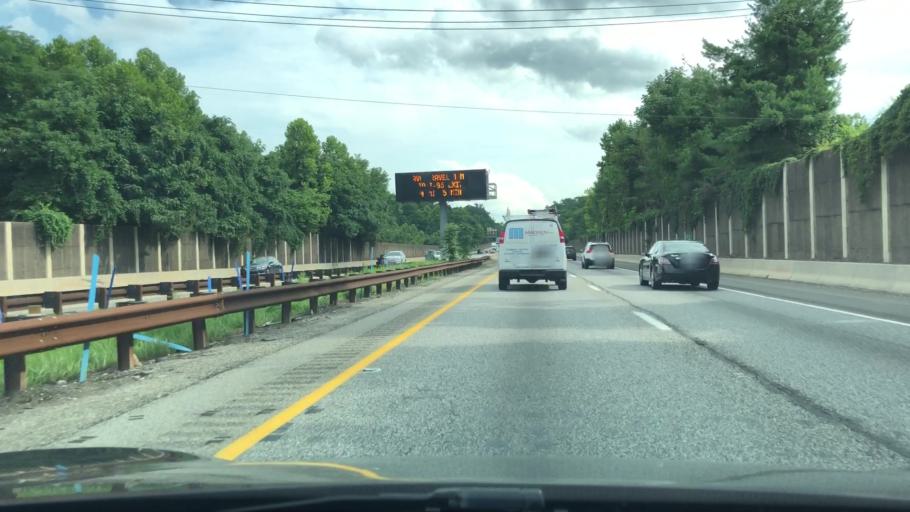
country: US
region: Pennsylvania
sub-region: Delaware County
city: Media
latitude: 39.9258
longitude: -75.3626
